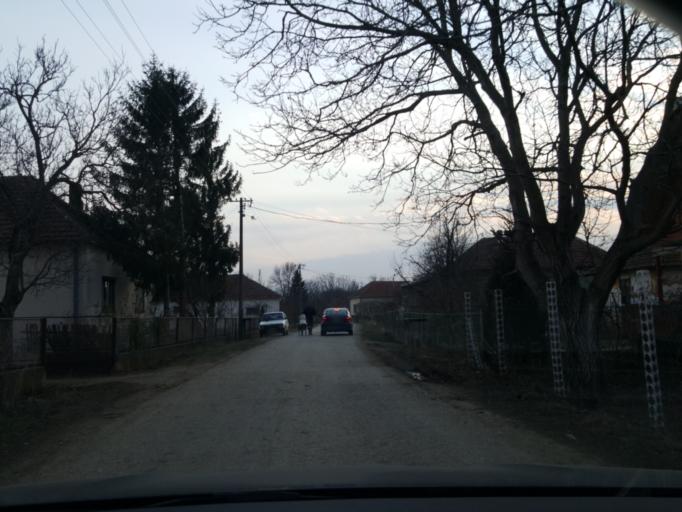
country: RS
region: Central Serbia
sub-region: Nisavski Okrug
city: Aleksinac
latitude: 43.5805
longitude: 21.6468
